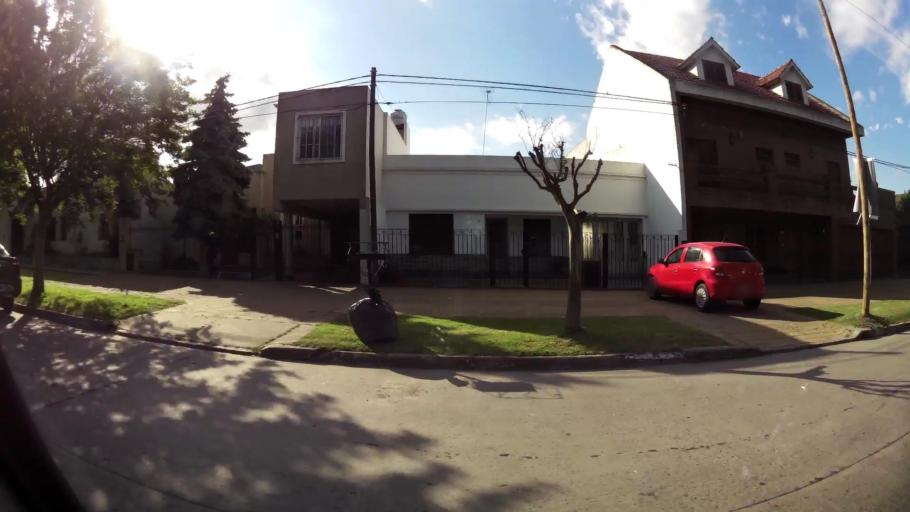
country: AR
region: Buenos Aires
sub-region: Partido de La Plata
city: La Plata
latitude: -34.8906
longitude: -57.9590
